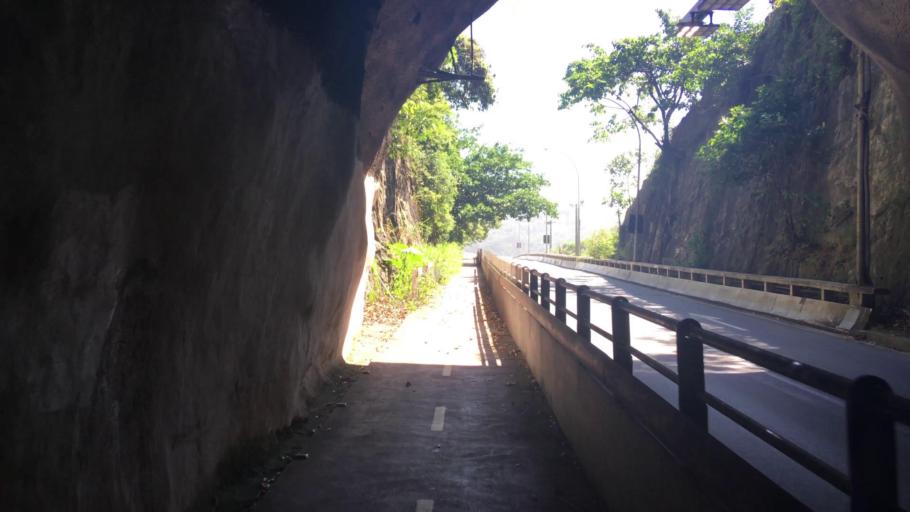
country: BR
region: Rio de Janeiro
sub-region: Rio De Janeiro
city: Rio de Janeiro
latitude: -23.0041
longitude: -43.2777
